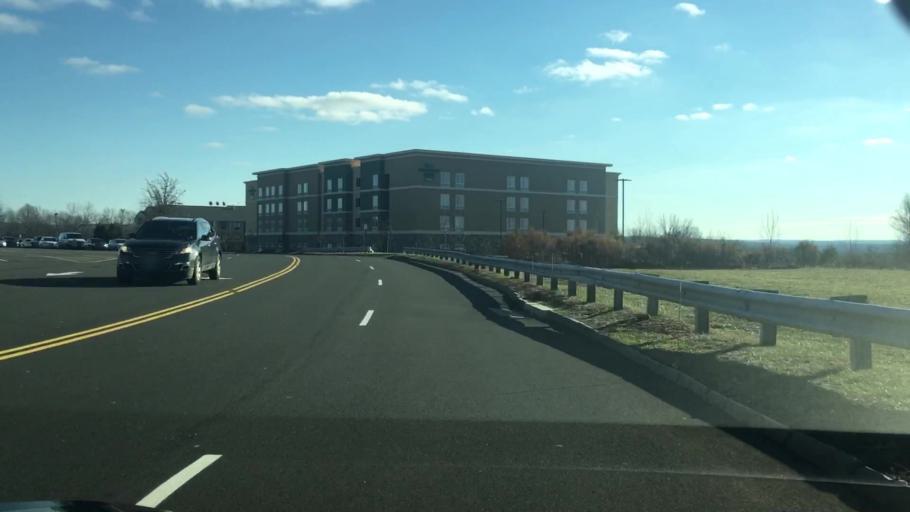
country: US
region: Connecticut
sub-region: Hartford County
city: Manchester
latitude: 41.8063
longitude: -72.5489
